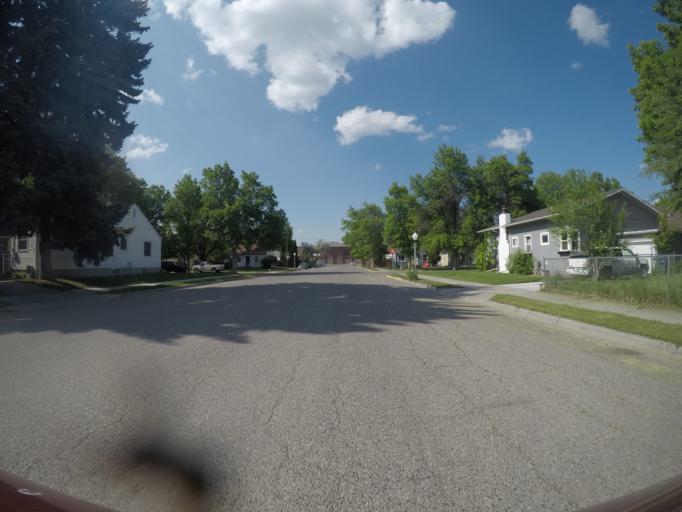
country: US
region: Montana
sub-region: Yellowstone County
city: Billings
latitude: 45.7827
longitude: -108.5254
